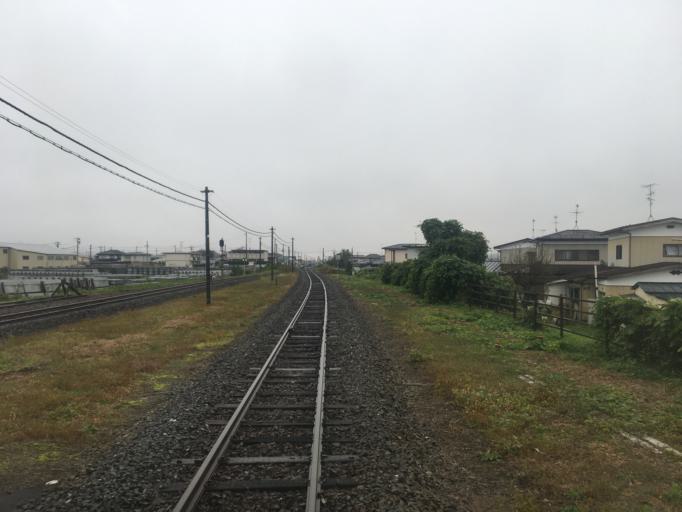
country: JP
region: Miyagi
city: Furukawa
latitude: 38.6519
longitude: 140.8720
